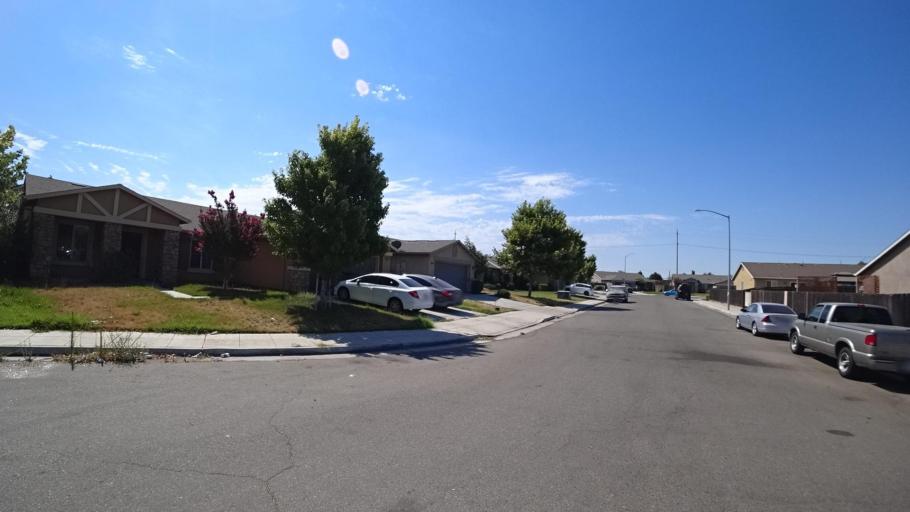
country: US
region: California
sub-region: Fresno County
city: Sunnyside
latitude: 36.7090
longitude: -119.7143
